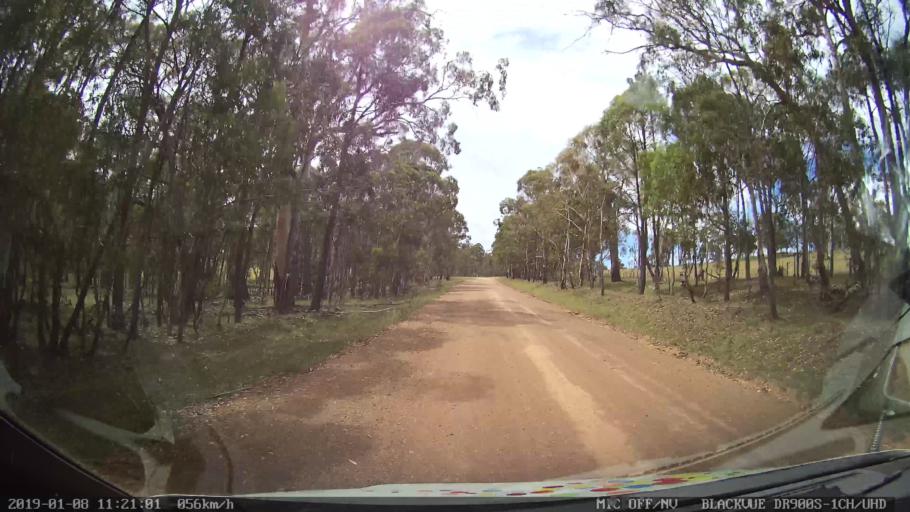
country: AU
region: New South Wales
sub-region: Guyra
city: Guyra
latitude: -30.2343
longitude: 151.5650
